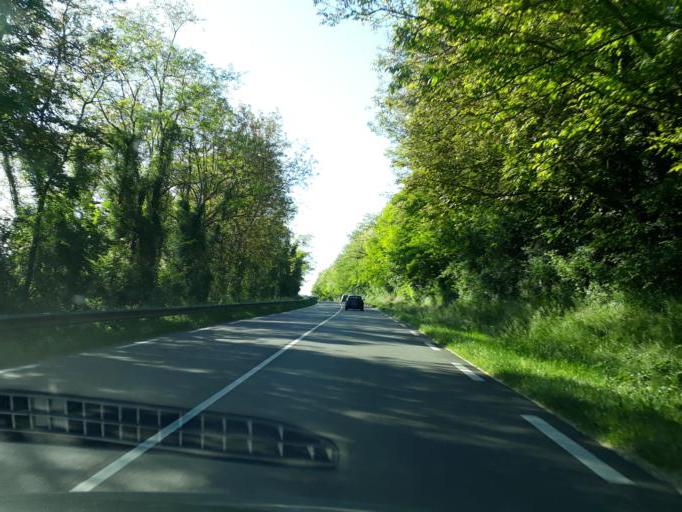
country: FR
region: Bourgogne
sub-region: Departement de la Nievre
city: Neuvy-sur-Loire
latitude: 47.5000
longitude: 2.9081
